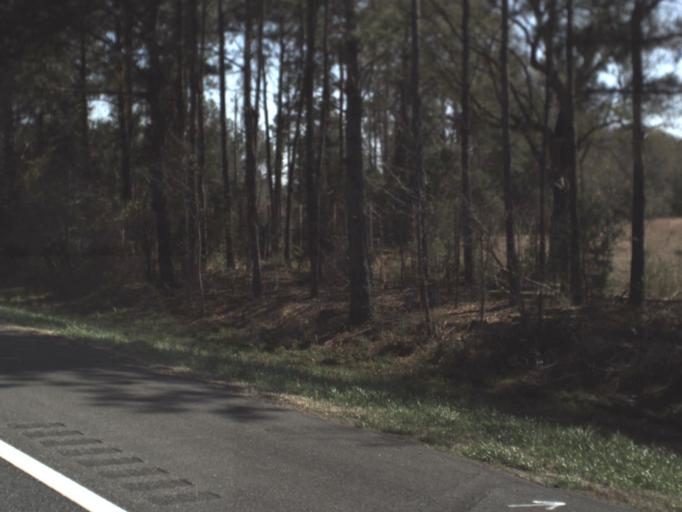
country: US
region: Florida
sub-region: Jackson County
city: Marianna
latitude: 30.7440
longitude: -85.2534
